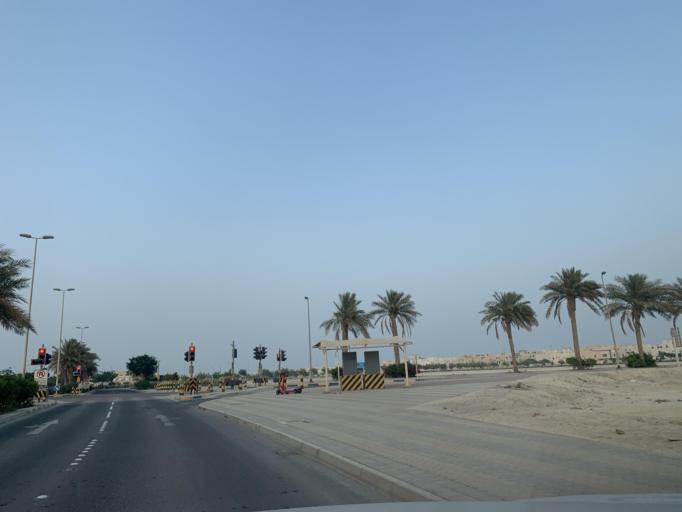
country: BH
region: Manama
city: Jidd Hafs
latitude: 26.2241
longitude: 50.4411
